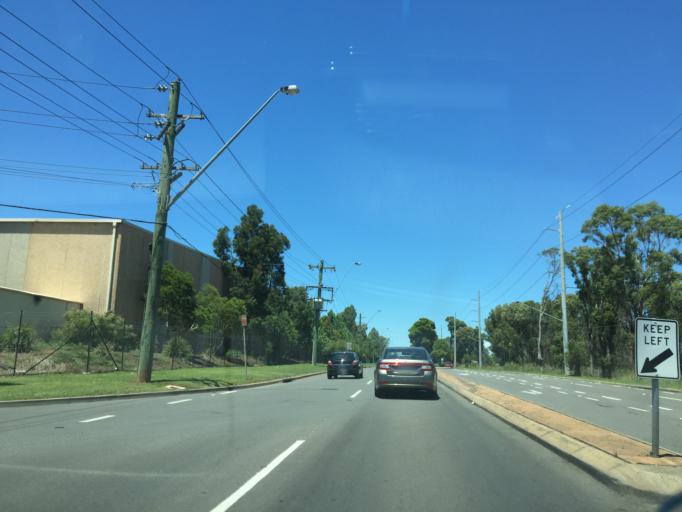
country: AU
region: New South Wales
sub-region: Blacktown
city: Doonside
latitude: -33.7873
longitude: 150.8720
